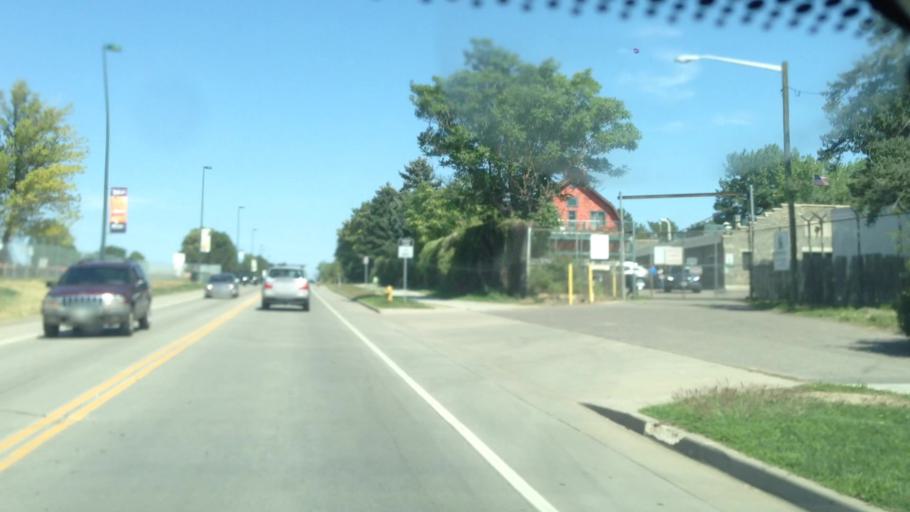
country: US
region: Colorado
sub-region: Denver County
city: Denver
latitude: 39.7512
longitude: -104.9546
